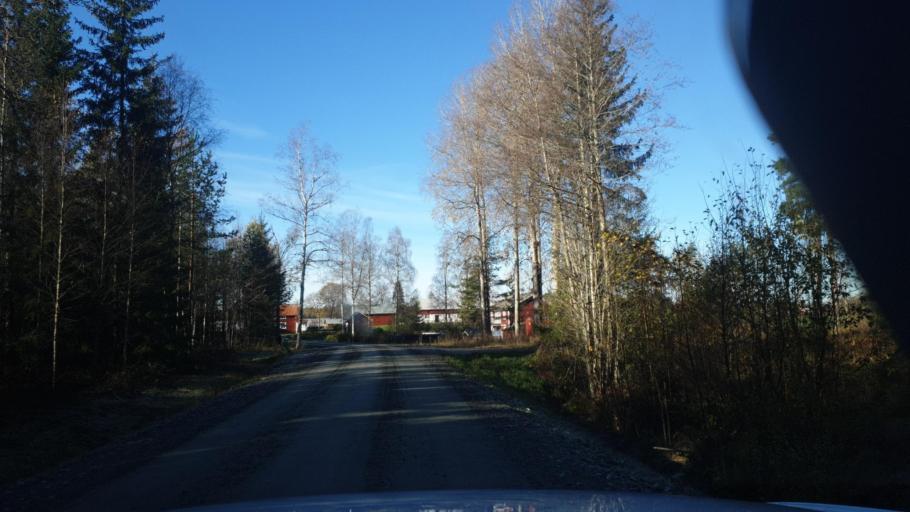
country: SE
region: Vaermland
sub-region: Karlstads Kommun
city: Edsvalla
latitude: 59.4515
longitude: 13.1474
